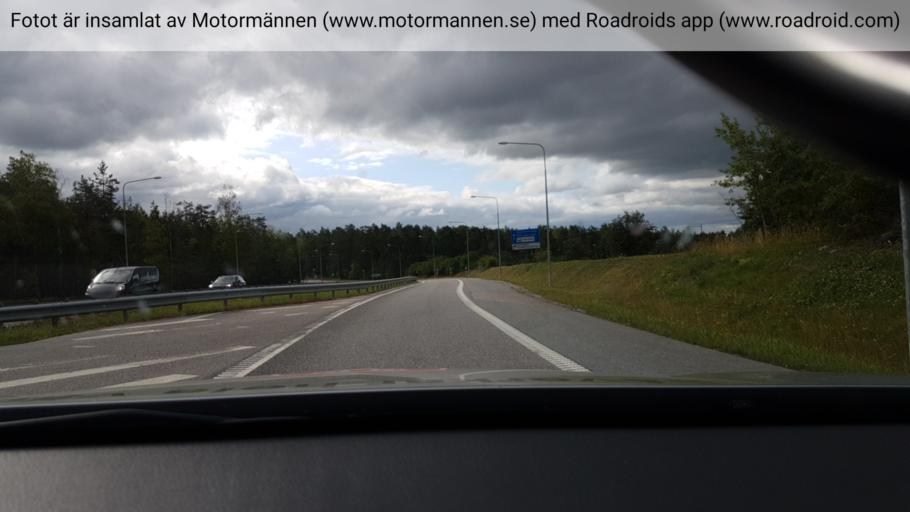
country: SE
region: Stockholm
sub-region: Nacka Kommun
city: Alta
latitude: 59.2420
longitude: 18.1847
